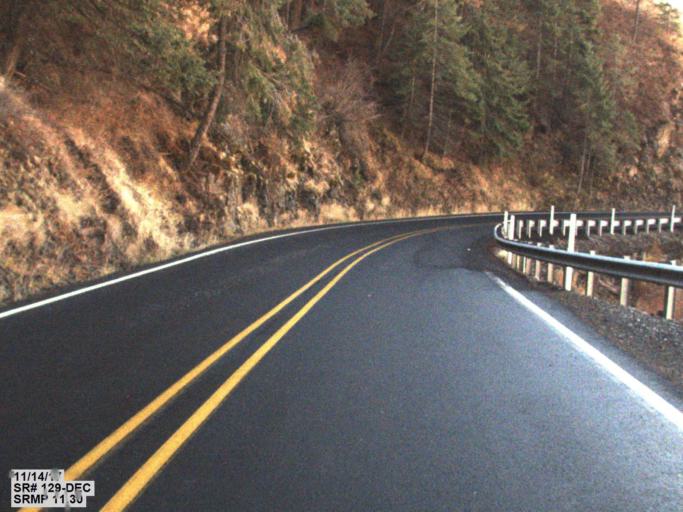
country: US
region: Washington
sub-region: Asotin County
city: Asotin
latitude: 46.0769
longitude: -117.2041
